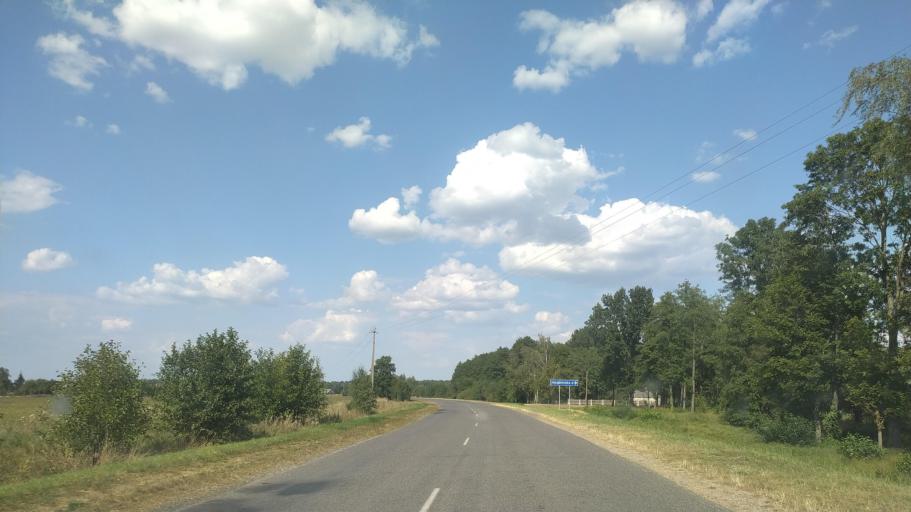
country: BY
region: Brest
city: Drahichyn
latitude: 52.1342
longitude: 25.1229
